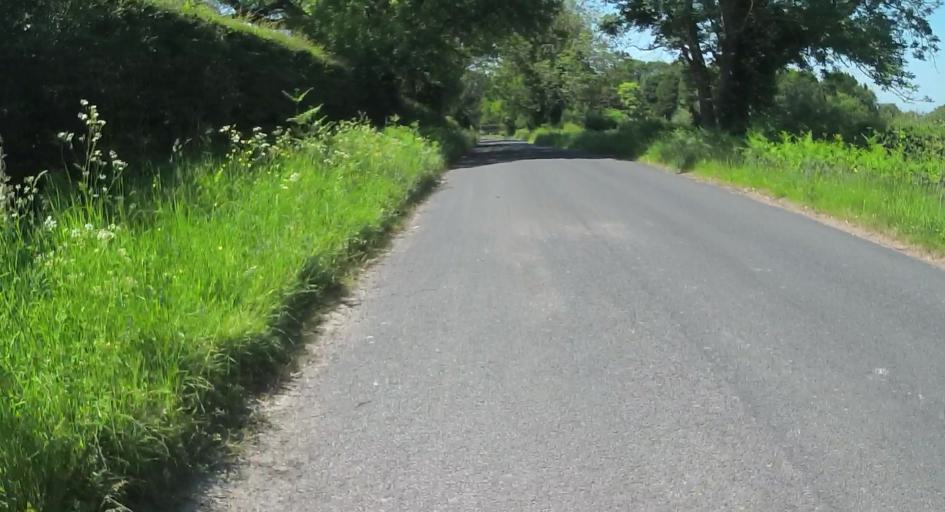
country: GB
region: England
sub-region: Hampshire
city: Kingsclere
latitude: 51.3460
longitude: -1.2048
